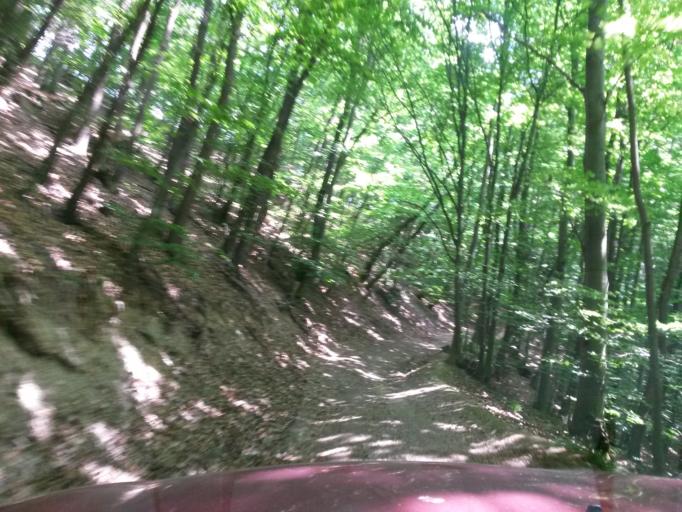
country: SK
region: Kosicky
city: Kosice
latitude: 48.7381
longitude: 21.1182
